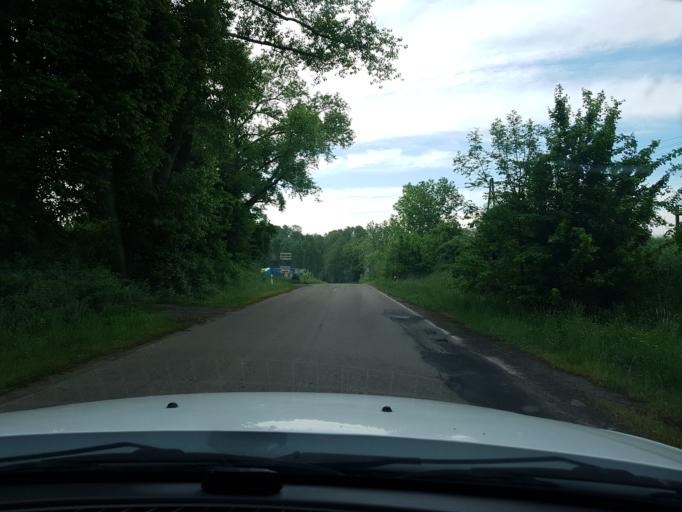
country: PL
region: West Pomeranian Voivodeship
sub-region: Powiat stargardzki
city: Chociwel
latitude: 53.4698
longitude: 15.3548
